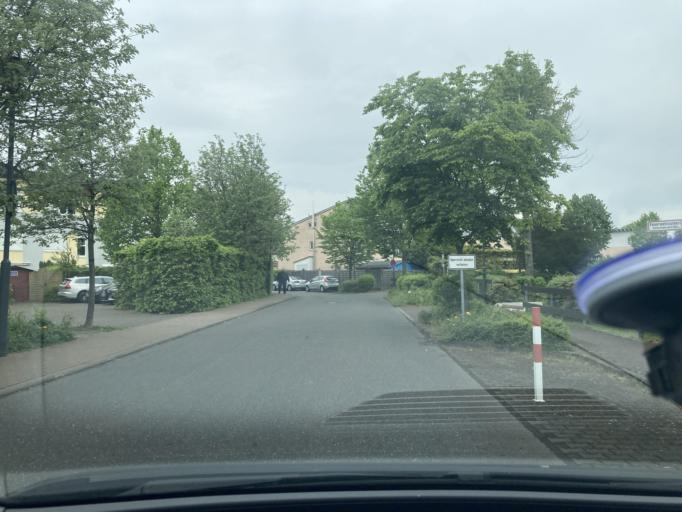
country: DE
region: Hesse
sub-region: Regierungsbezirk Darmstadt
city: Eschborn
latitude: 50.1442
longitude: 8.5783
